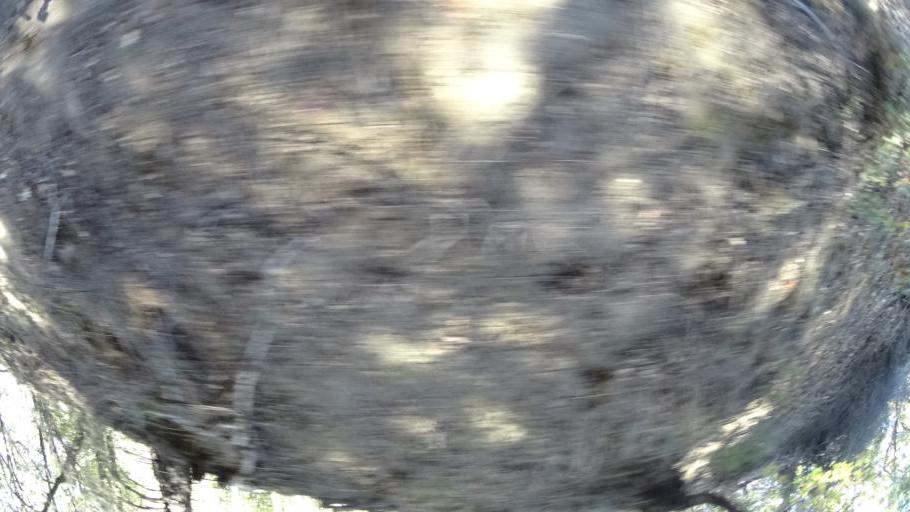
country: US
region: California
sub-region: Humboldt County
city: Willow Creek
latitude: 41.2773
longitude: -123.2761
